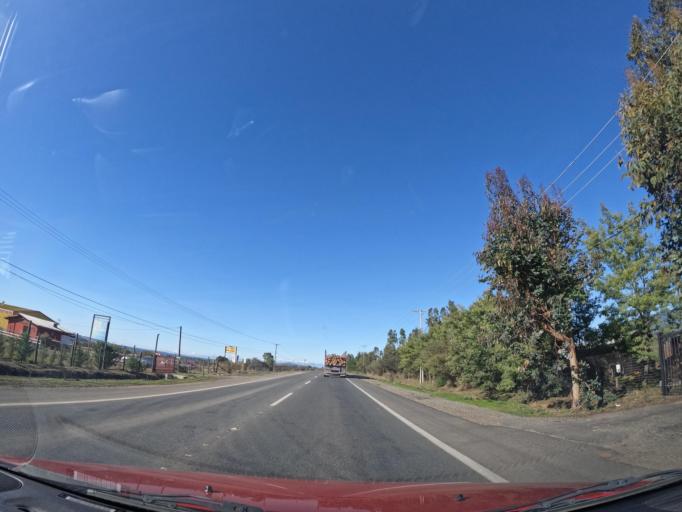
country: CL
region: Maule
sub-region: Provincia de Cauquenes
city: Cauquenes
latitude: -35.9621
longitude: -72.2480
